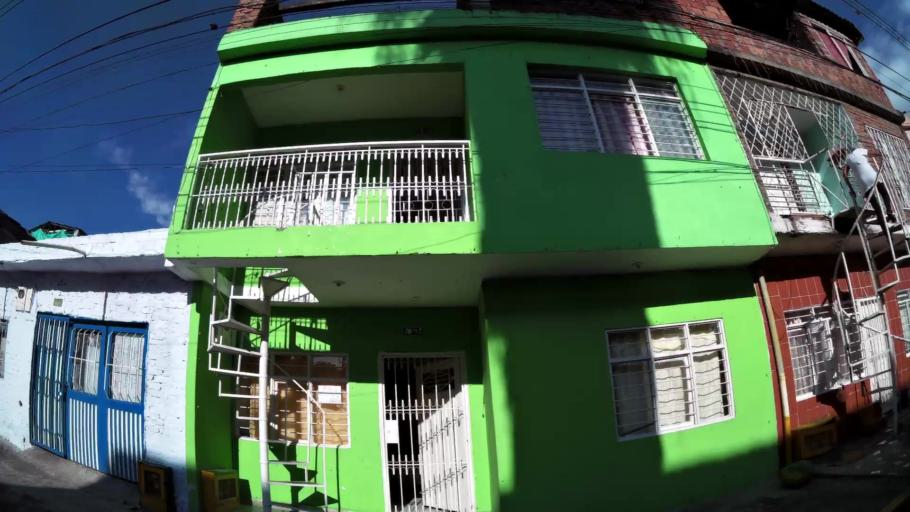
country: CO
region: Valle del Cauca
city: Cali
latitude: 3.4269
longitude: -76.5085
